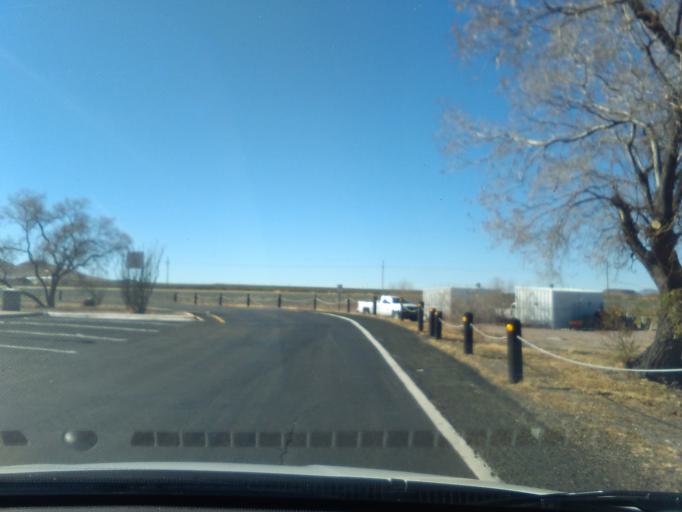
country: US
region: New Mexico
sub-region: Hidalgo County
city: Lordsburg
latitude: 32.3527
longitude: -108.7432
